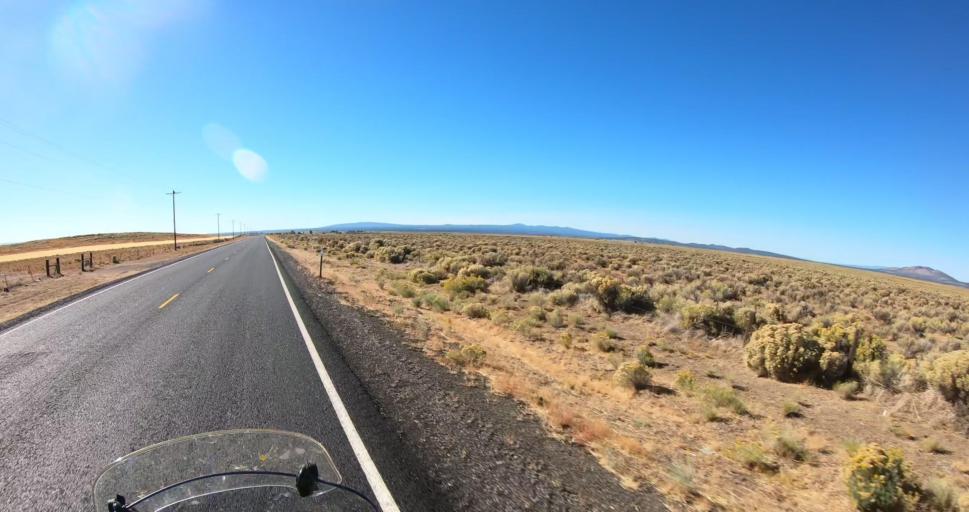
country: US
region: Oregon
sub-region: Deschutes County
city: La Pine
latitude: 43.1288
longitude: -120.9629
